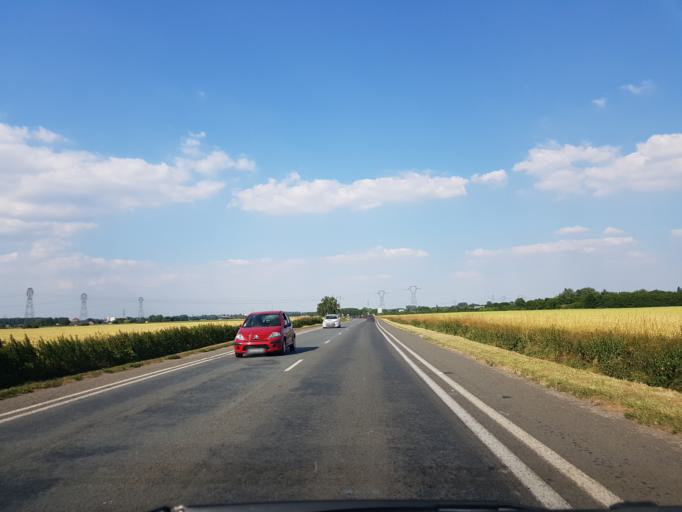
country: FR
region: Nord-Pas-de-Calais
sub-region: Departement du Nord
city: Camphin-en-Carembault
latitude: 50.5205
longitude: 2.9945
